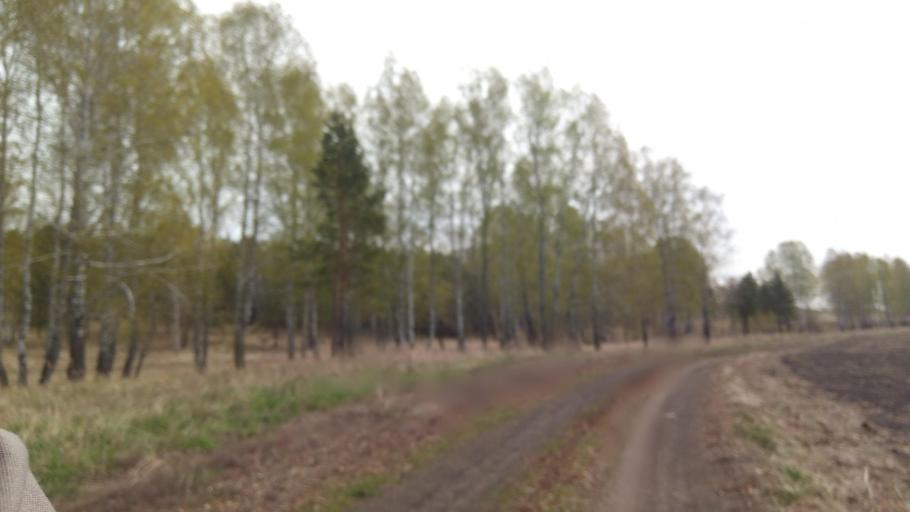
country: RU
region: Chelyabinsk
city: Timiryazevskiy
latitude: 55.0182
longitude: 60.8556
